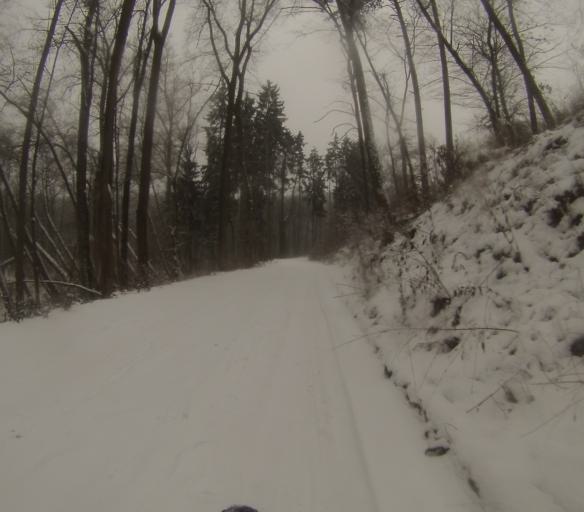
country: CZ
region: South Moravian
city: Orechov
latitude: 49.1349
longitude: 16.5271
